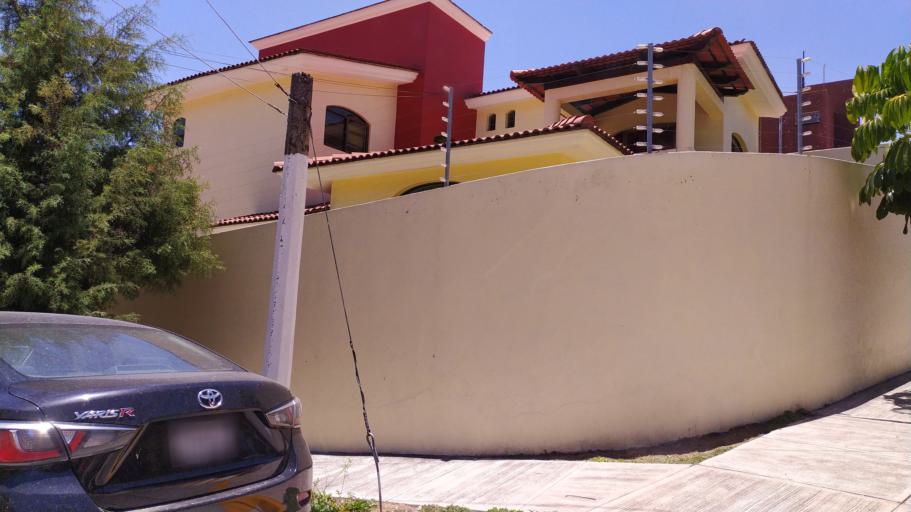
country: MX
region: Jalisco
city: Guadalajara
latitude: 20.6880
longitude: -103.3992
